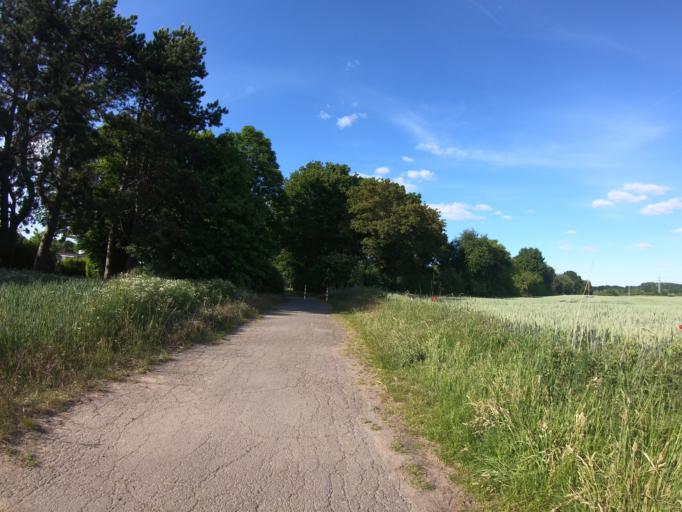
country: DE
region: Lower Saxony
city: Leiferde
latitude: 52.2203
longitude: 10.5374
